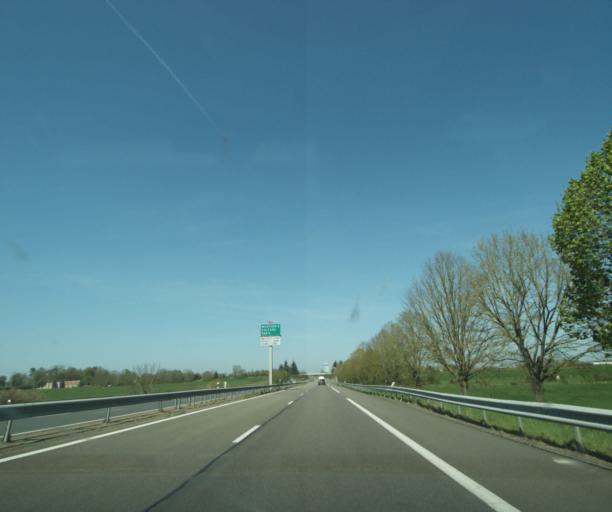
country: FR
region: Bourgogne
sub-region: Departement de la Nievre
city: La Charite-sur-Loire
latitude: 47.1809
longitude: 3.0405
